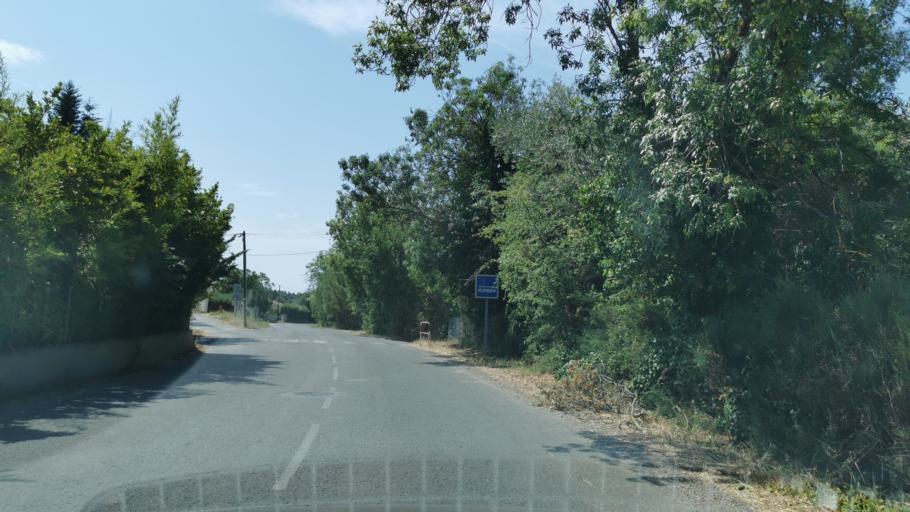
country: FR
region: Languedoc-Roussillon
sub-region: Departement de l'Aude
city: Bize-Minervois
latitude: 43.3101
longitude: 2.8709
